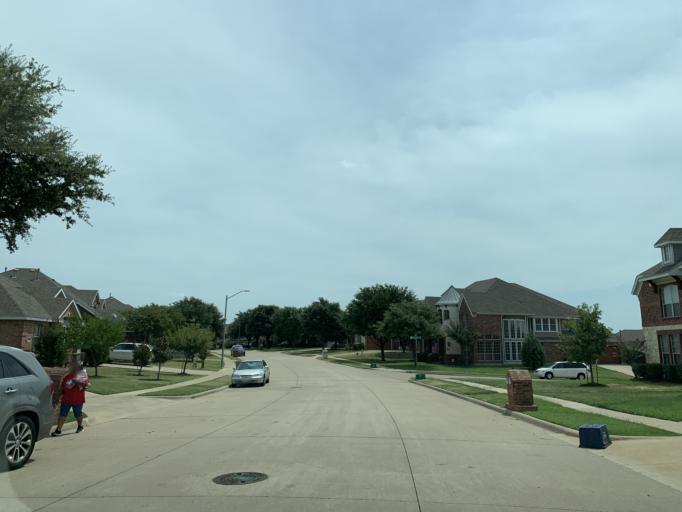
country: US
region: Texas
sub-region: Dallas County
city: Cedar Hill
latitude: 32.6504
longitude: -97.0025
